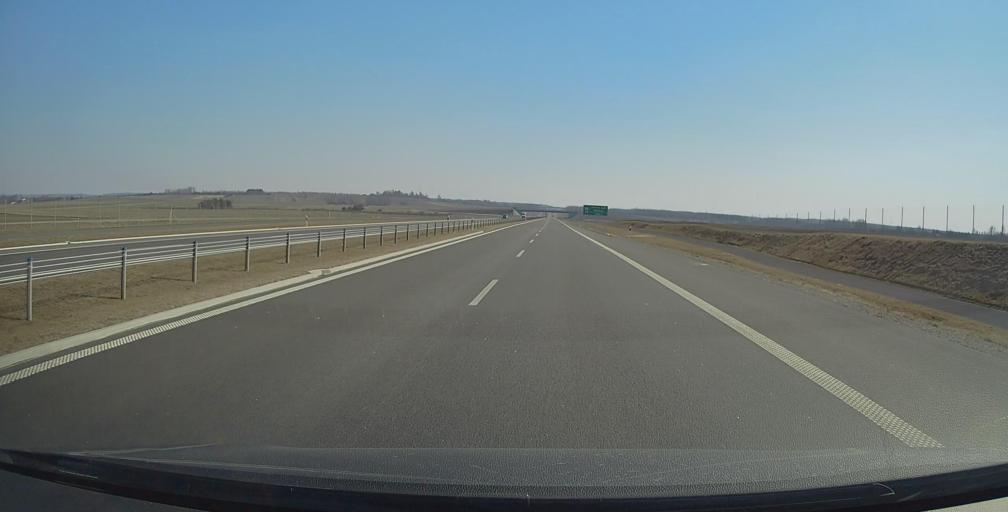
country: PL
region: Lublin Voivodeship
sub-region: Powiat janowski
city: Modliborzyce
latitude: 50.7429
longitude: 22.3073
